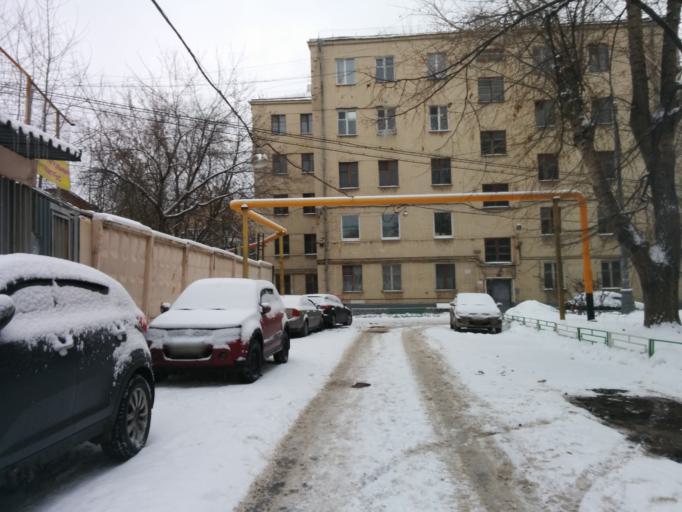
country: RU
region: Moscow
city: Zamoskvorech'ye
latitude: 55.7103
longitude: 37.6157
